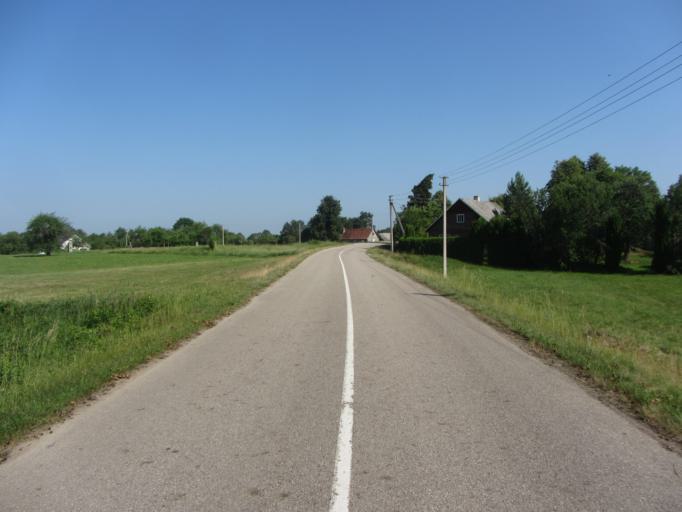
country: LT
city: Veisiejai
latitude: 54.1883
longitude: 23.6808
